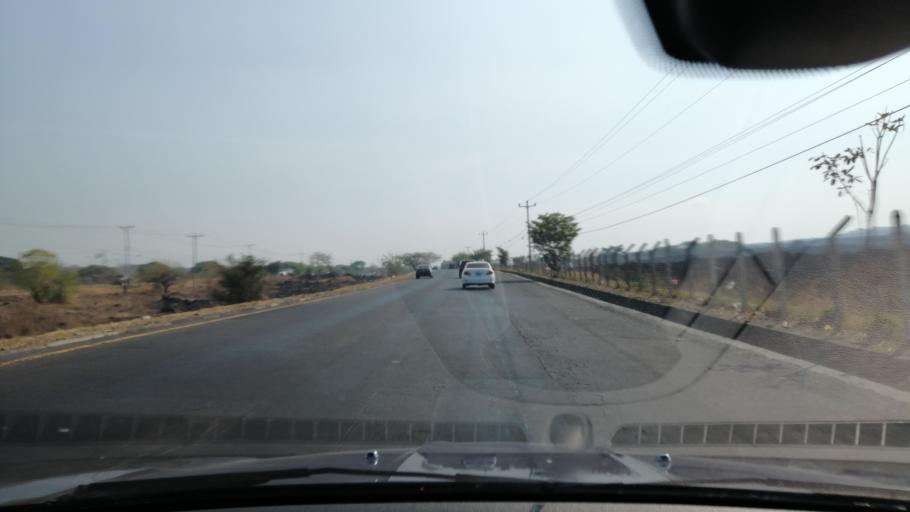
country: SV
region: La Libertad
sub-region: Distrito de Quezaltepeque
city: Quezaltepeque
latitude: 13.8015
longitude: -89.3344
